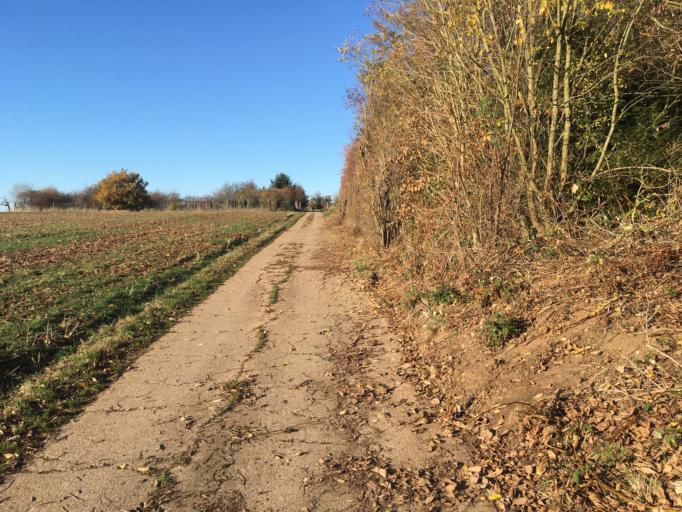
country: DE
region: Hesse
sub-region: Regierungsbezirk Darmstadt
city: Langenselbold
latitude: 50.1851
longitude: 9.0220
